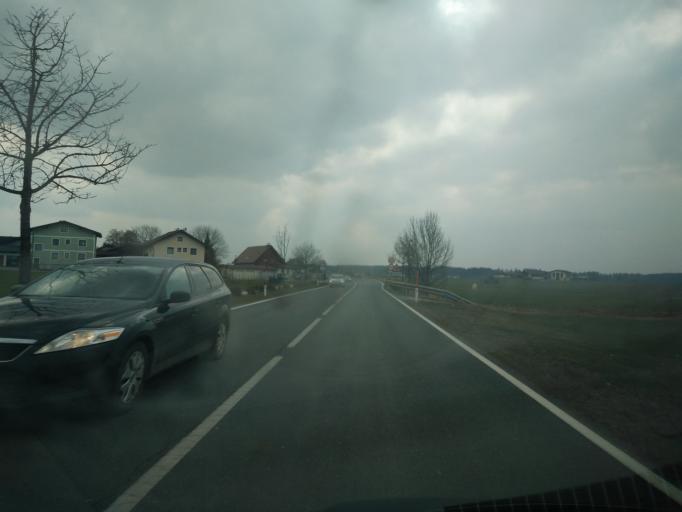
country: AT
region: Salzburg
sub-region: Politischer Bezirk Salzburg-Umgebung
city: Lamprechtshausen
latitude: 47.9780
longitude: 12.9520
